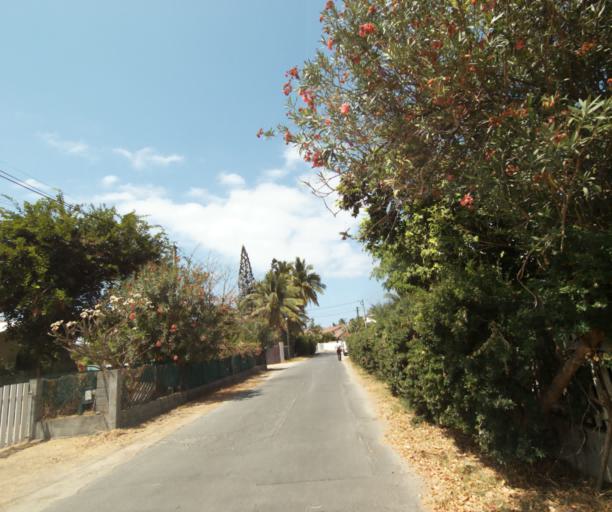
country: RE
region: Reunion
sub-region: Reunion
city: Trois-Bassins
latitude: -21.0885
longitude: 55.2317
